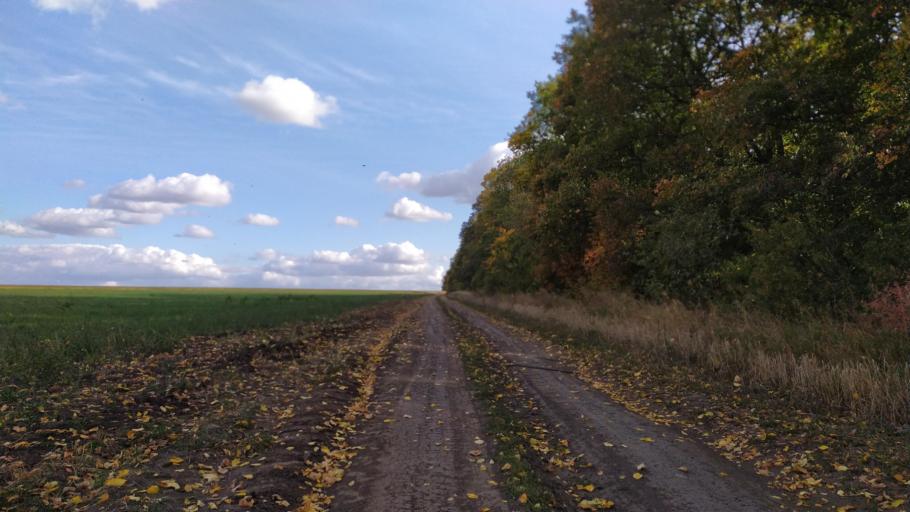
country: RU
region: Kursk
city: Kursk
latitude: 51.6192
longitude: 36.1627
